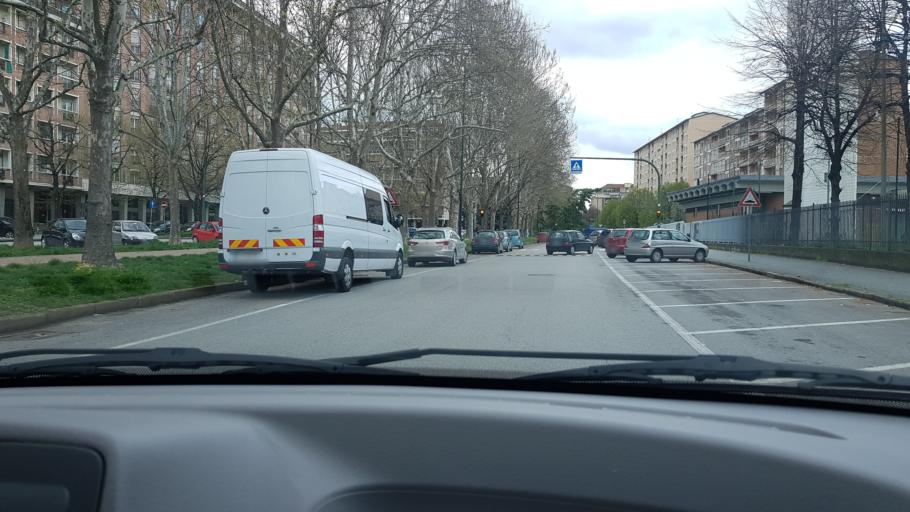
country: IT
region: Piedmont
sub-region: Provincia di Torino
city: Nichelino
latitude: 45.0153
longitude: 7.6328
